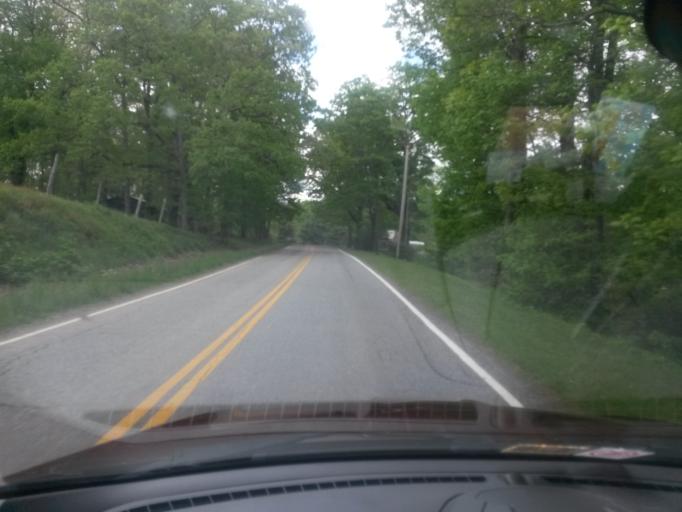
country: US
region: Virginia
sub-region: Floyd County
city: Floyd
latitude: 36.7712
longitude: -80.3867
